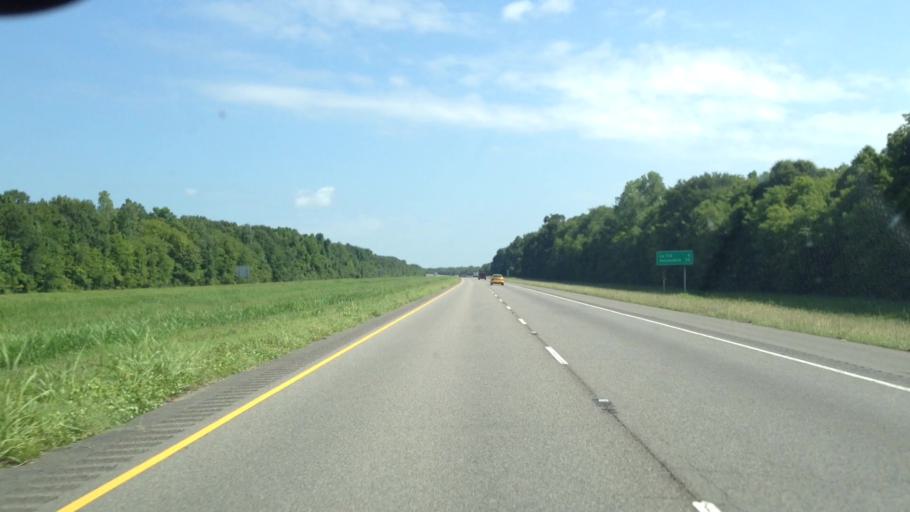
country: US
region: Louisiana
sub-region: Avoyelles Parish
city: Bunkie
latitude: 30.8799
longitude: -92.2271
